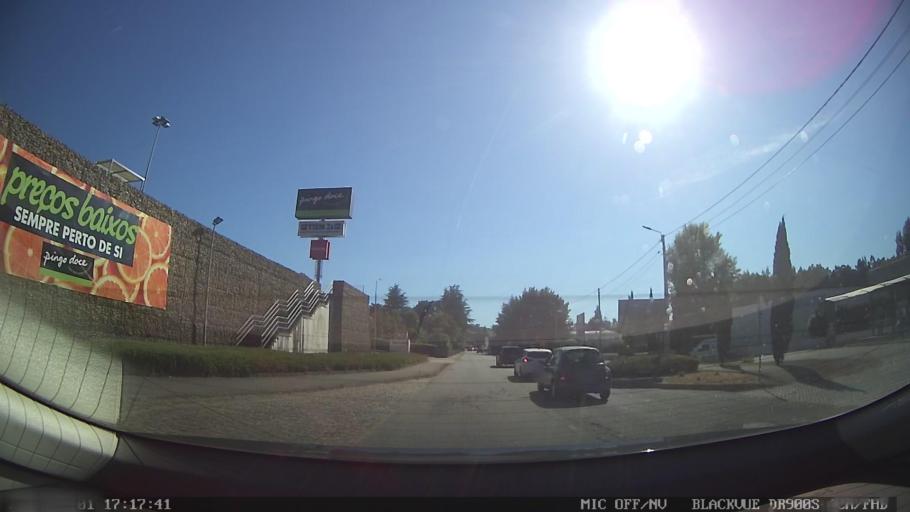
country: PT
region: Porto
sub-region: Santo Tirso
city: Santo Tirso
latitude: 41.3398
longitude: -8.4950
